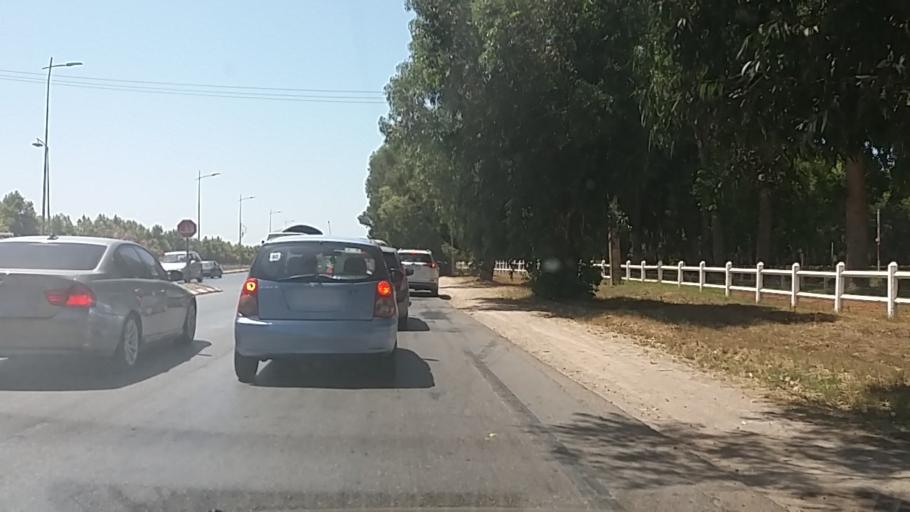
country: MA
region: Rabat-Sale-Zemmour-Zaer
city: Sale
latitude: 34.0290
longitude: -6.7343
